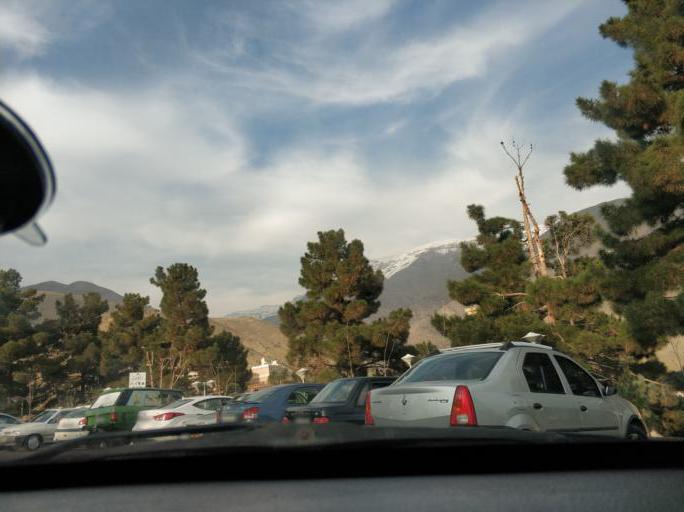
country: IR
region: Tehran
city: Tajrish
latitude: 35.8151
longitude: 51.4880
